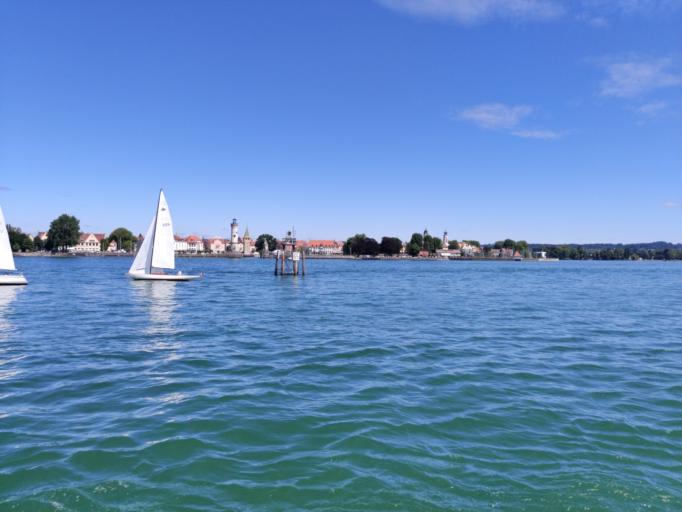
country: DE
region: Bavaria
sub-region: Swabia
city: Lindau
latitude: 47.5388
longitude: 9.6844
